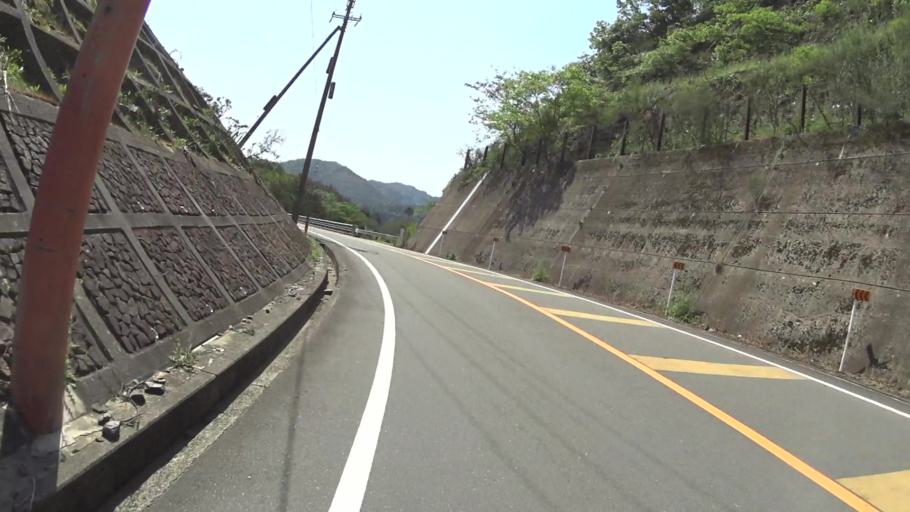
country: JP
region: Kyoto
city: Kameoka
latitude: 35.1334
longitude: 135.5544
